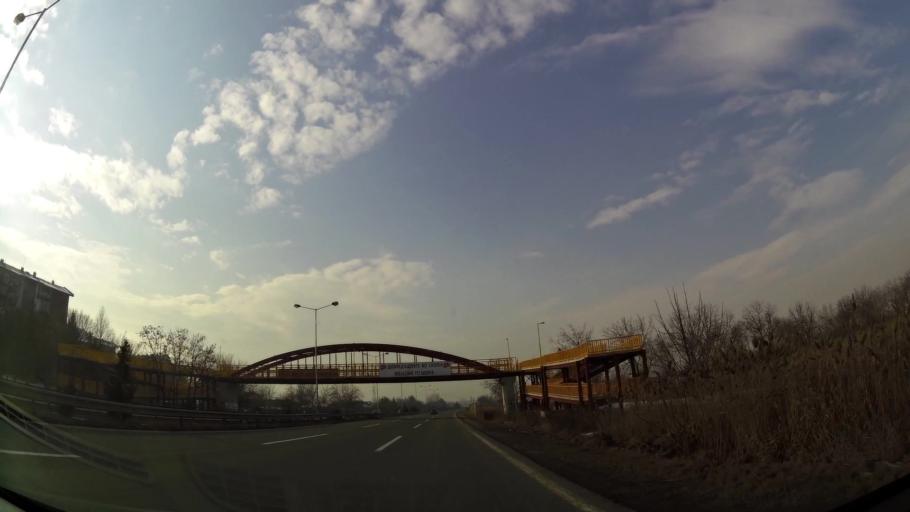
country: MK
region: Kisela Voda
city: Kisela Voda
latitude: 41.9976
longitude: 21.5115
